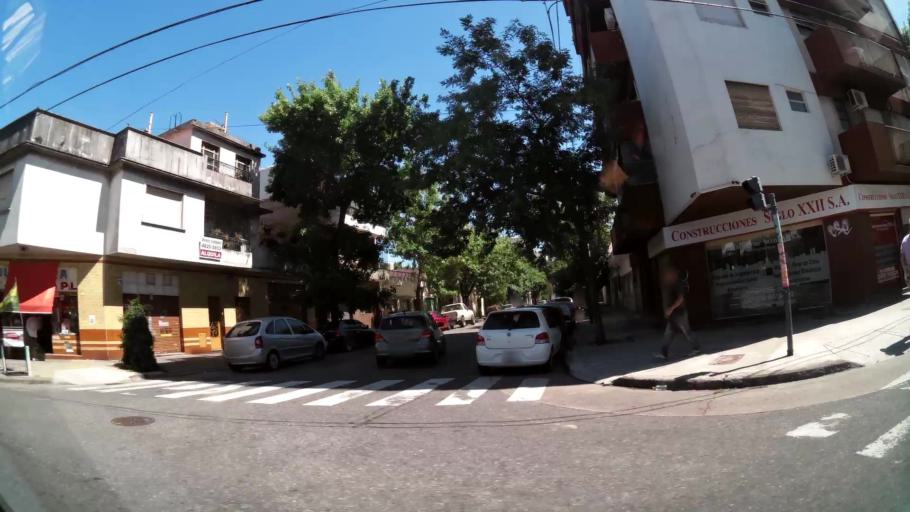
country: AR
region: Buenos Aires F.D.
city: Buenos Aires
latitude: -34.6364
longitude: -58.4145
